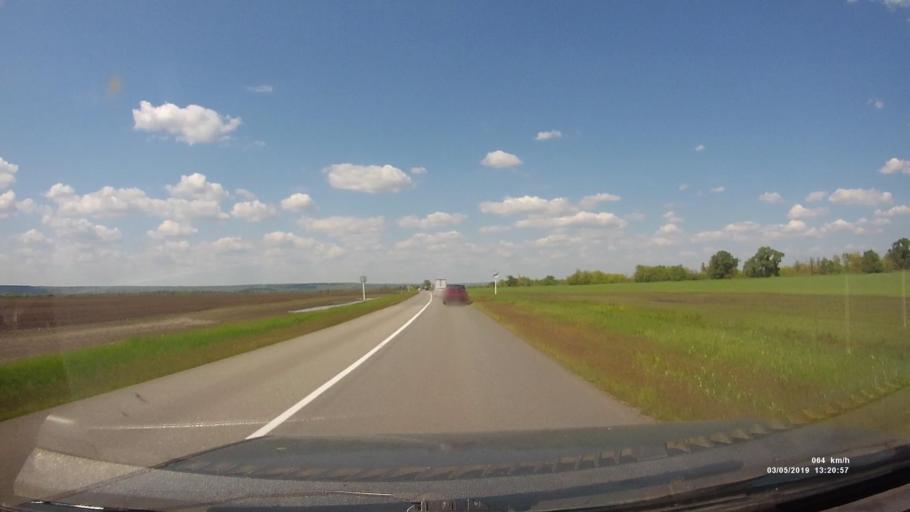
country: RU
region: Rostov
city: Semikarakorsk
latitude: 47.5503
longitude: 40.7502
